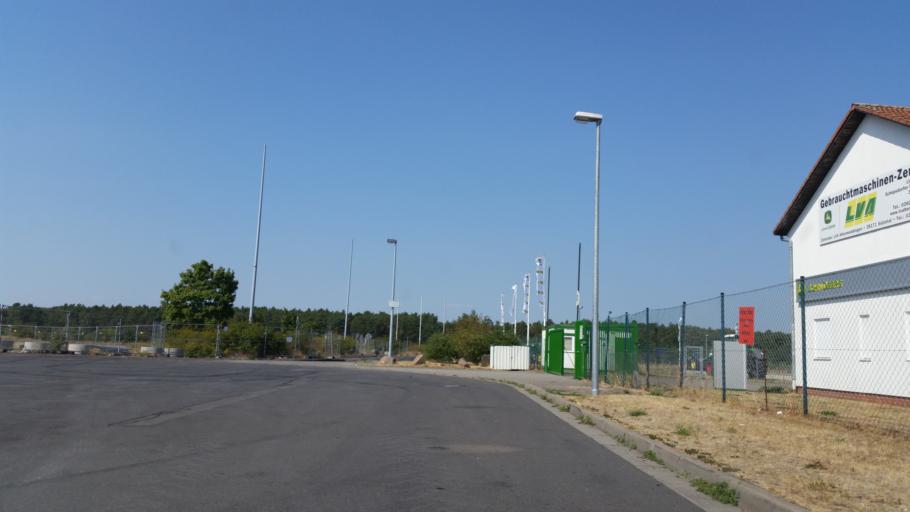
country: DE
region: Brandenburg
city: Ziesar
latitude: 52.2478
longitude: 12.2505
